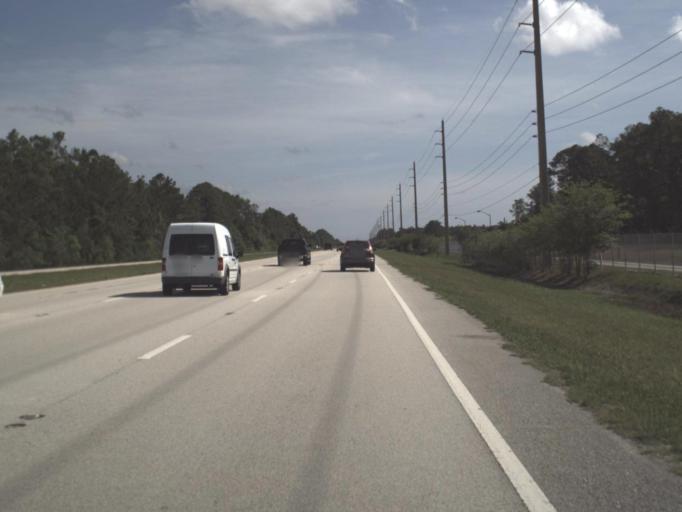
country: US
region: Florida
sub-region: Clay County
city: Orange Park
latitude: 30.2061
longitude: -81.7064
